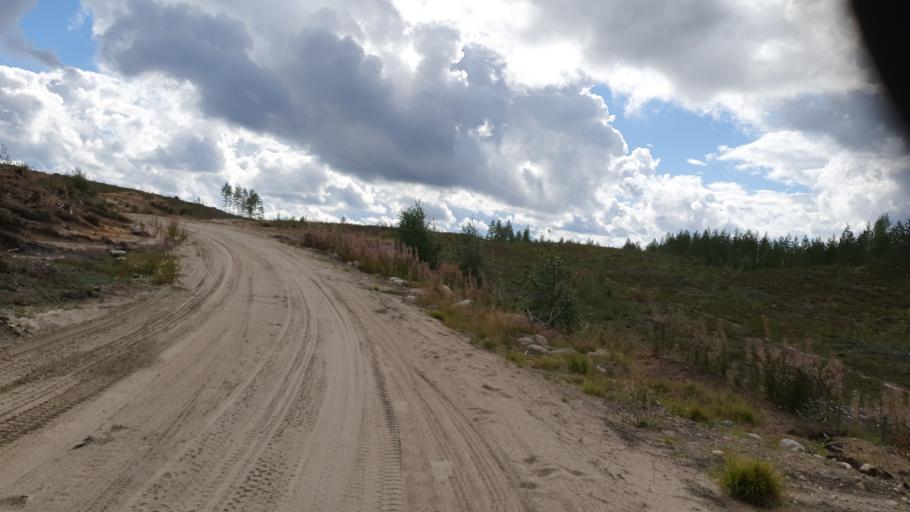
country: FI
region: Kainuu
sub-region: Kehys-Kainuu
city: Kuhmo
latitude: 64.1508
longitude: 29.3693
